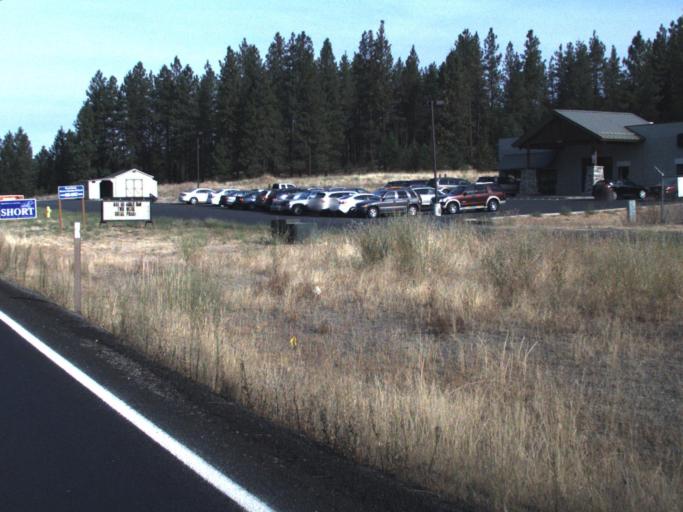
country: US
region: Washington
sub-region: Spokane County
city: Deer Park
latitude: 47.8223
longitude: -117.5891
